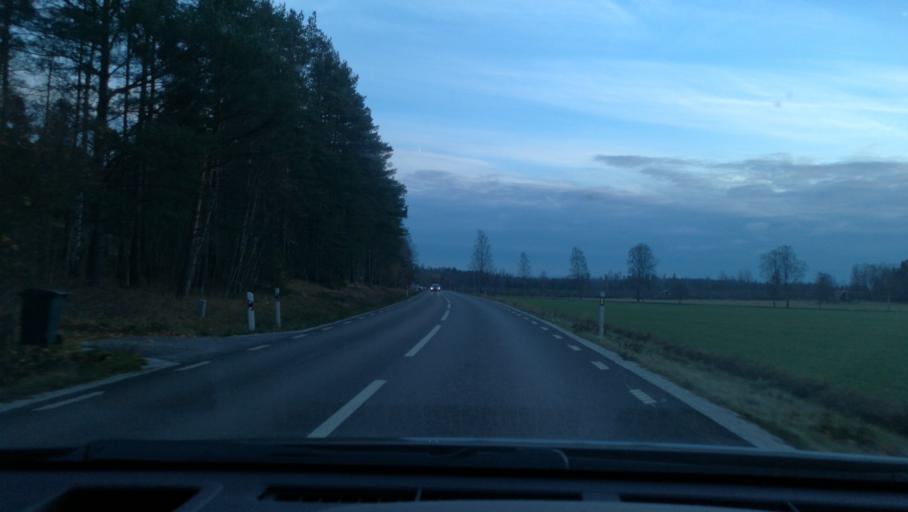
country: SE
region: Soedermanland
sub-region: Vingakers Kommun
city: Vingaker
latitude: 59.1105
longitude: 15.8179
